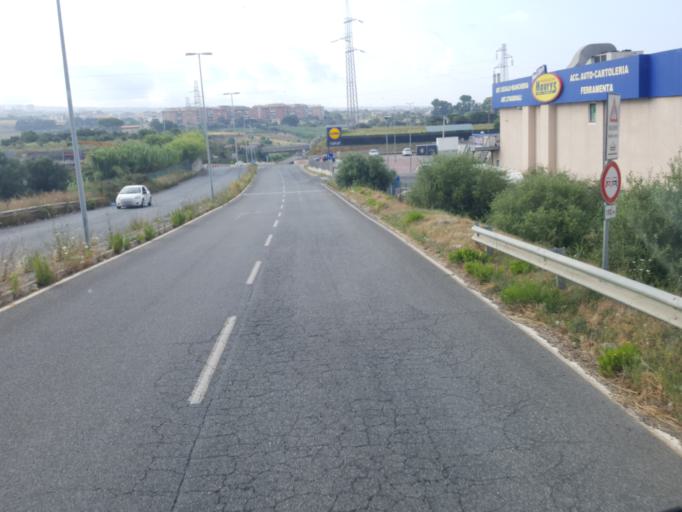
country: IT
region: Latium
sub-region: Citta metropolitana di Roma Capitale
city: Civitavecchia
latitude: 42.1083
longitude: 11.7867
